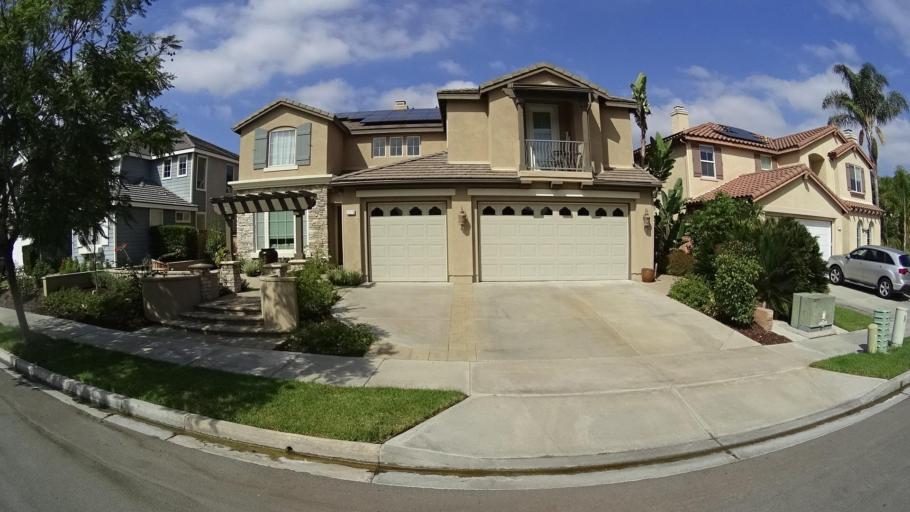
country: US
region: California
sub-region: San Diego County
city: Fairbanks Ranch
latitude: 33.0066
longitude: -117.1081
